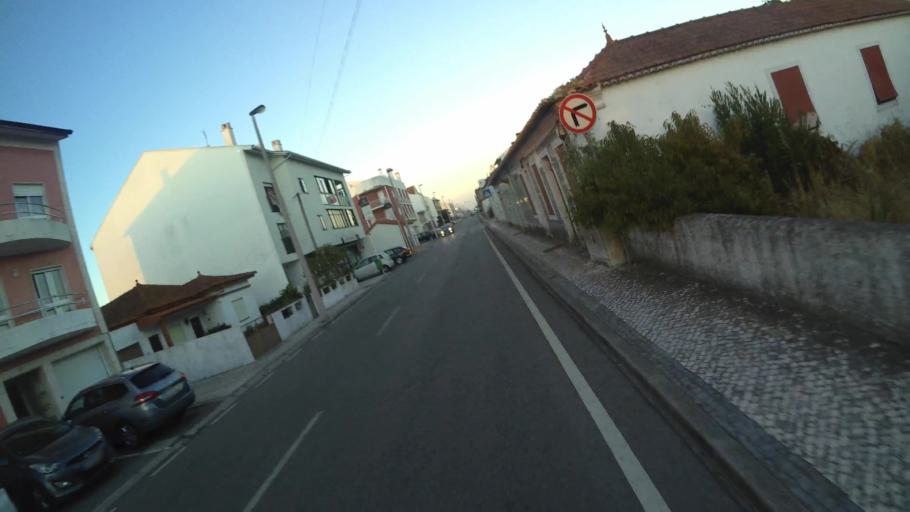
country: PT
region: Aveiro
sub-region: Ilhavo
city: Gafanha da Nazare
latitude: 40.6376
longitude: -8.7178
